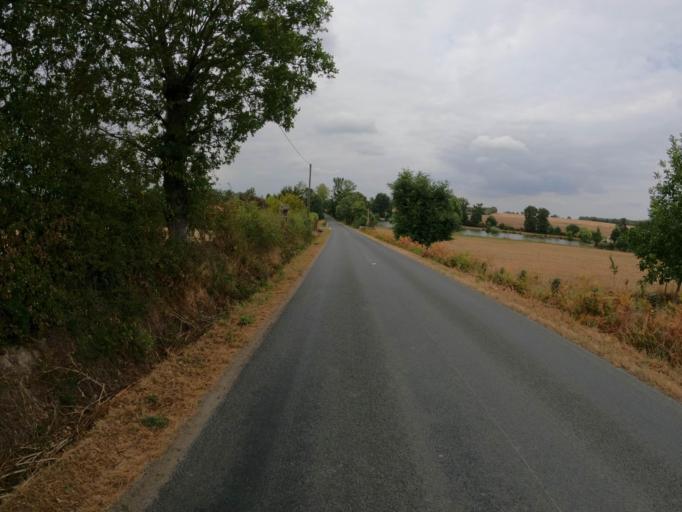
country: FR
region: Pays de la Loire
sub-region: Departement de la Vendee
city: Les Landes-Genusson
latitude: 46.9720
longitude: -1.1133
